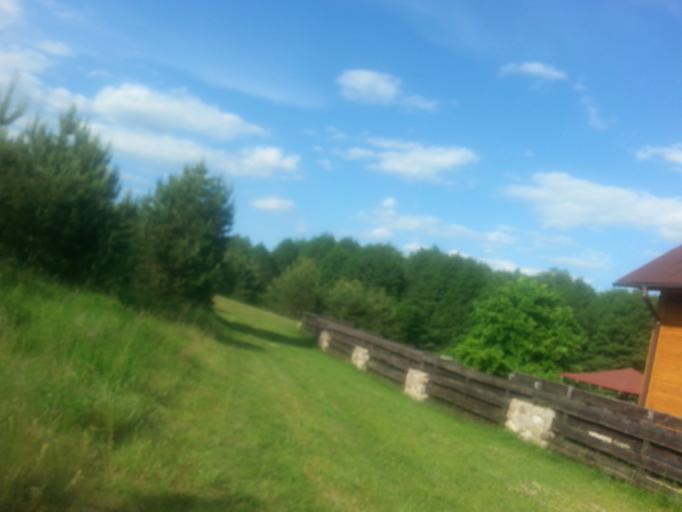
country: BY
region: Minsk
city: Narach
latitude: 54.9774
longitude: 26.6070
